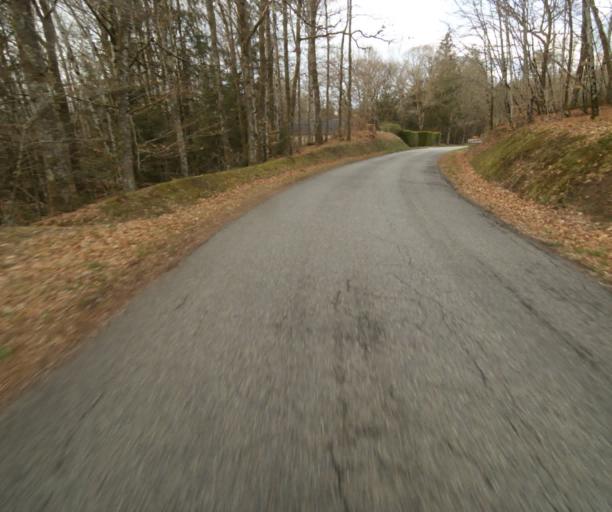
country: FR
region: Limousin
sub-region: Departement de la Correze
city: Argentat
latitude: 45.2236
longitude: 1.9778
